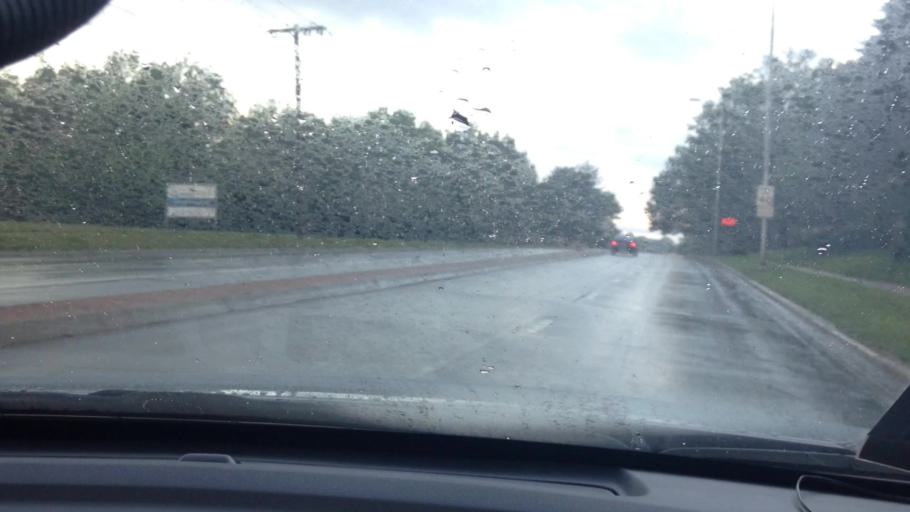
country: US
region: Kansas
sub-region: Johnson County
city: Overland Park
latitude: 38.9422
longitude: -94.6865
